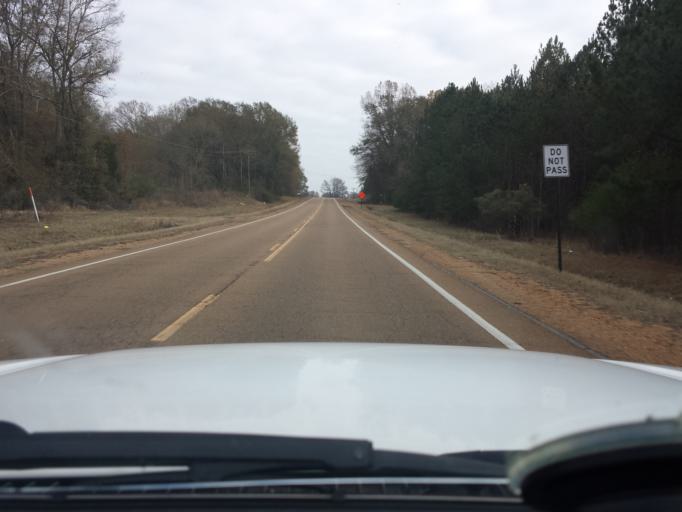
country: US
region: Mississippi
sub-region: Yazoo County
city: Yazoo City
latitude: 32.7916
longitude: -90.2072
